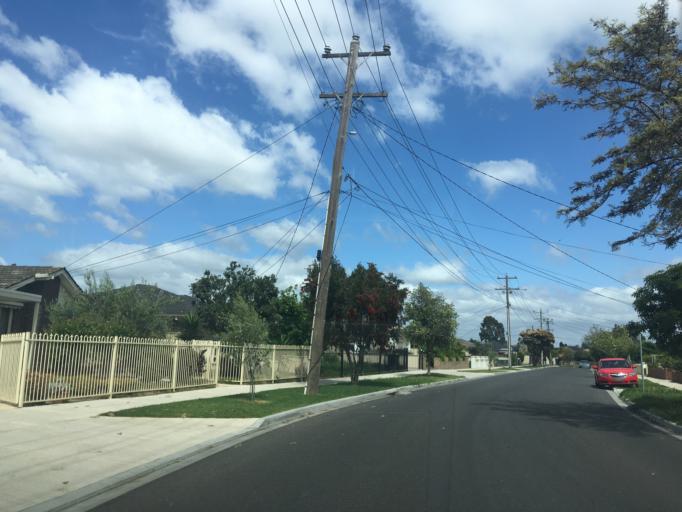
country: AU
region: Victoria
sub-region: Brimbank
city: Sunshine West
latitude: -37.7934
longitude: 144.8046
